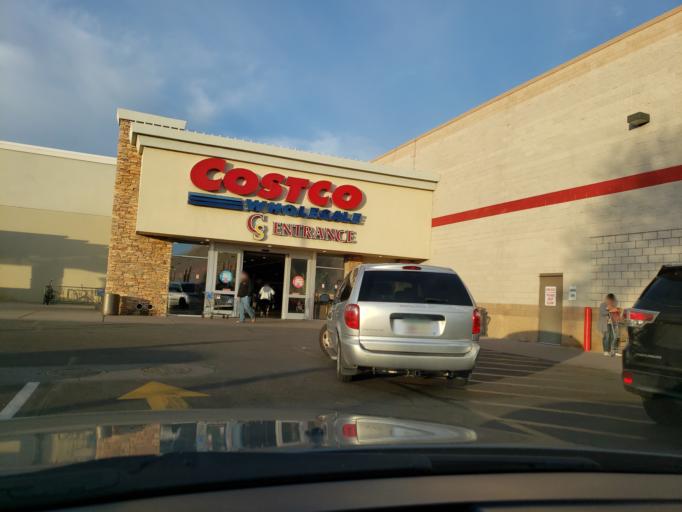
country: US
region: Arizona
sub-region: Maricopa County
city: Phoenix
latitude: 33.5217
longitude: -112.0961
